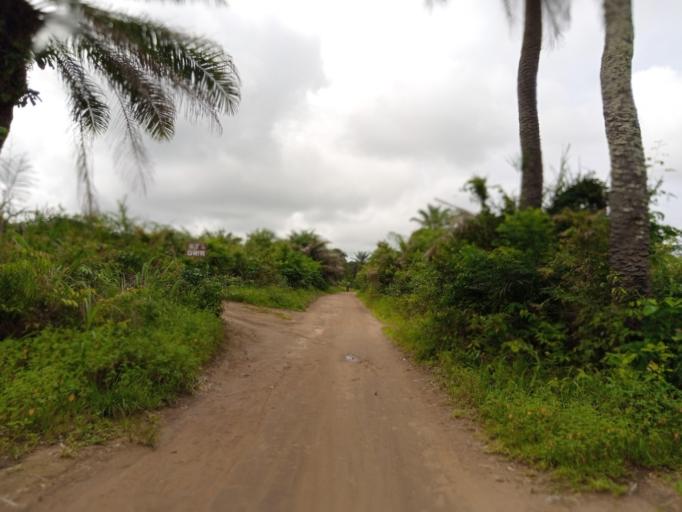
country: SL
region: Northern Province
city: Masoyila
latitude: 8.5820
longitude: -13.1908
